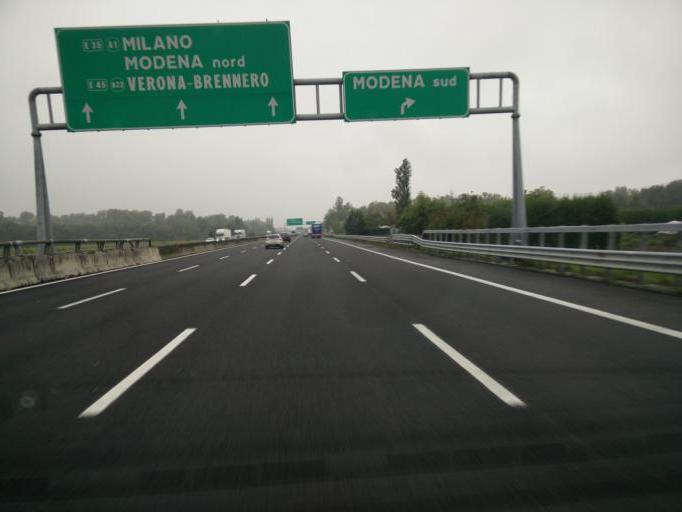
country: IT
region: Emilia-Romagna
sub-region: Provincia di Modena
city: San Vito
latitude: 44.5753
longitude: 10.9949
